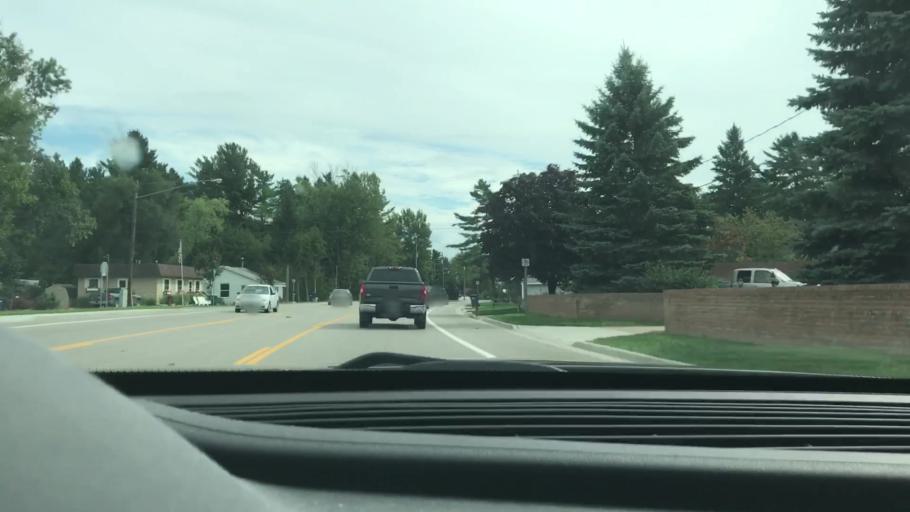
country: US
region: Michigan
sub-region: Missaukee County
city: Lake City
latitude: 44.3248
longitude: -85.2121
